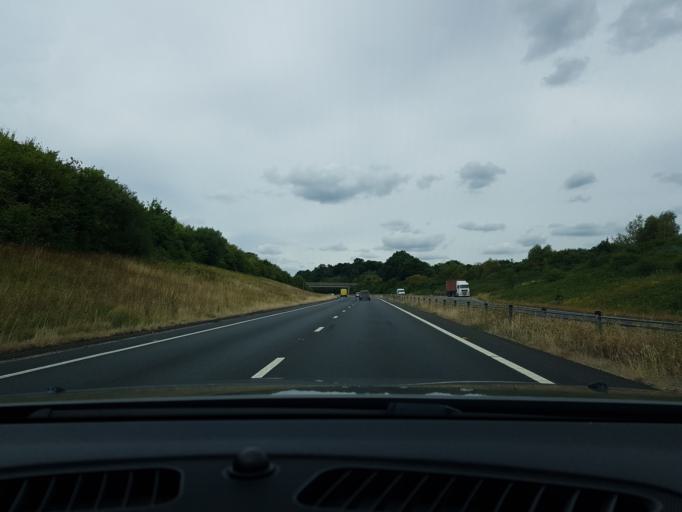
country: GB
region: England
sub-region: Hampshire
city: Highclere
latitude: 51.3725
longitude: -1.3641
